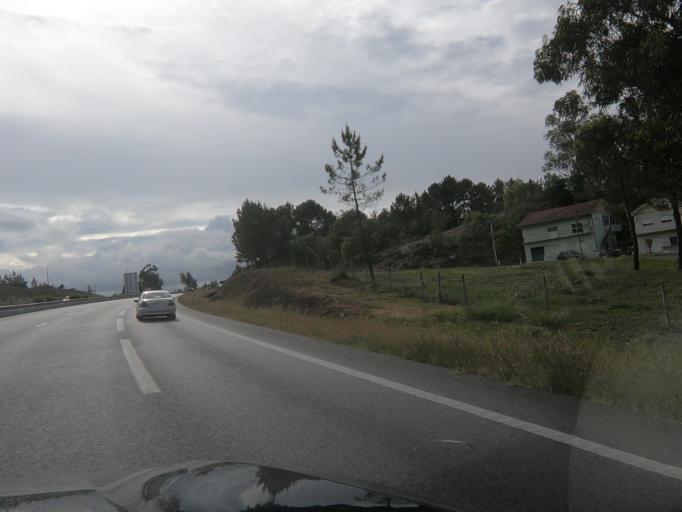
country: PT
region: Porto
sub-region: Valongo
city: Campo
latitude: 41.1880
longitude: -8.4708
